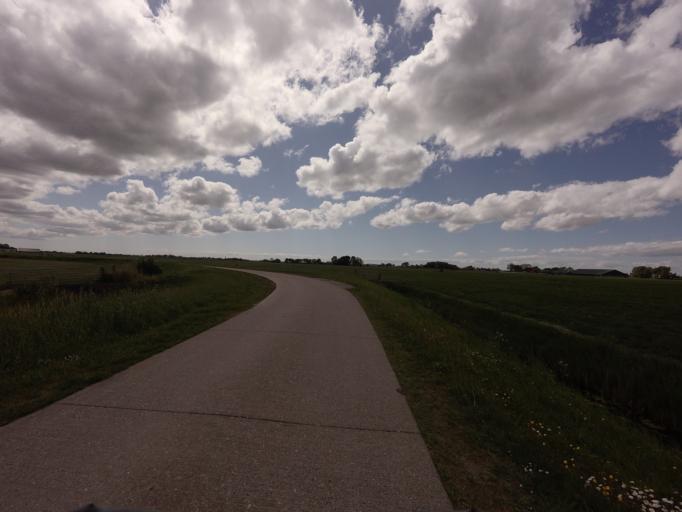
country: NL
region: Friesland
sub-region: Gemeente Franekeradeel
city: Tzum
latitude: 53.1278
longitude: 5.5522
